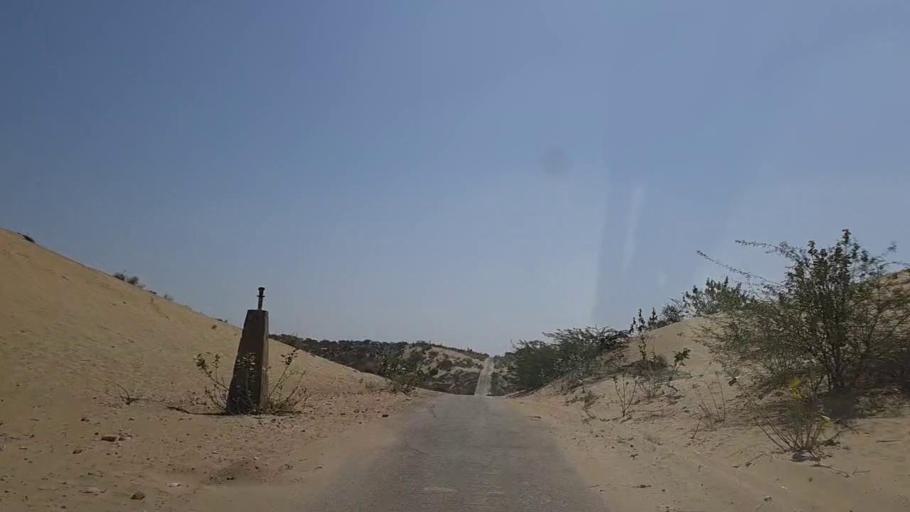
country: PK
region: Sindh
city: Diplo
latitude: 24.5091
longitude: 69.4226
